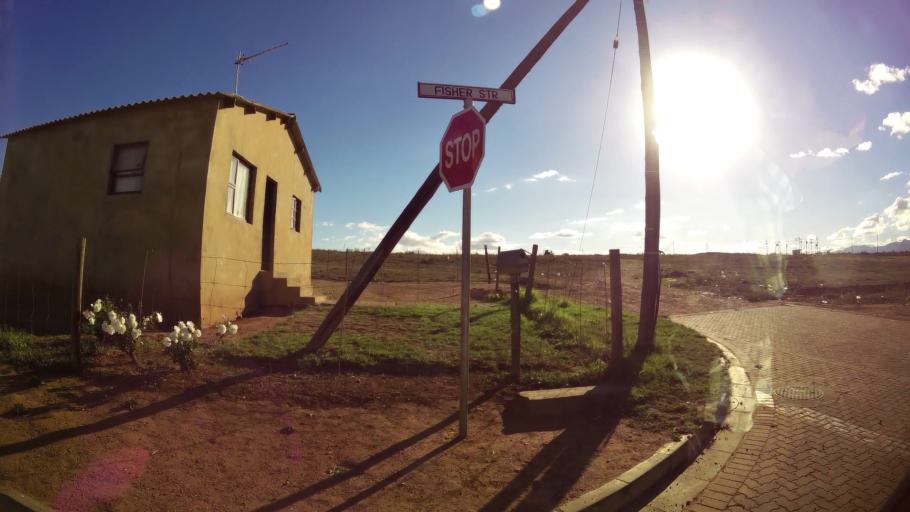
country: ZA
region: Western Cape
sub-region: Eden District Municipality
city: Riversdale
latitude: -34.1079
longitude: 20.9599
